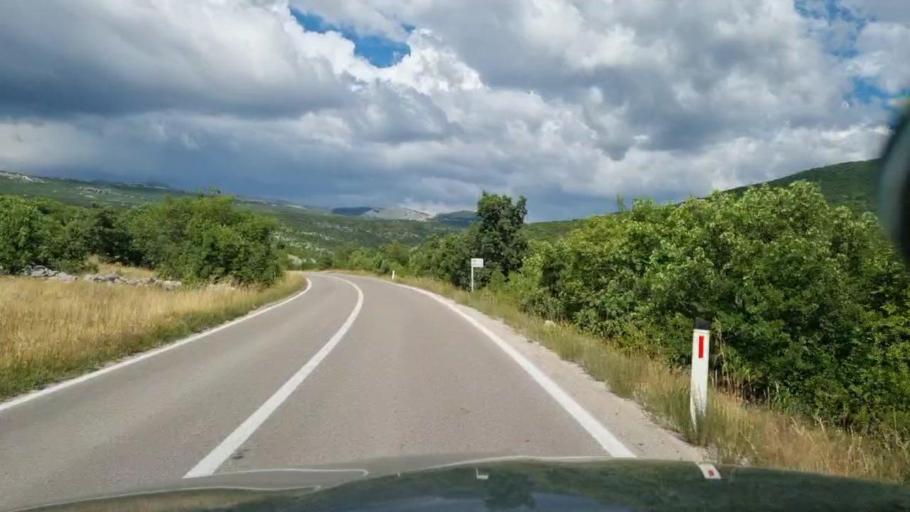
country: BA
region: Republika Srpska
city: Nevesinje
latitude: 43.2590
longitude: 18.0049
